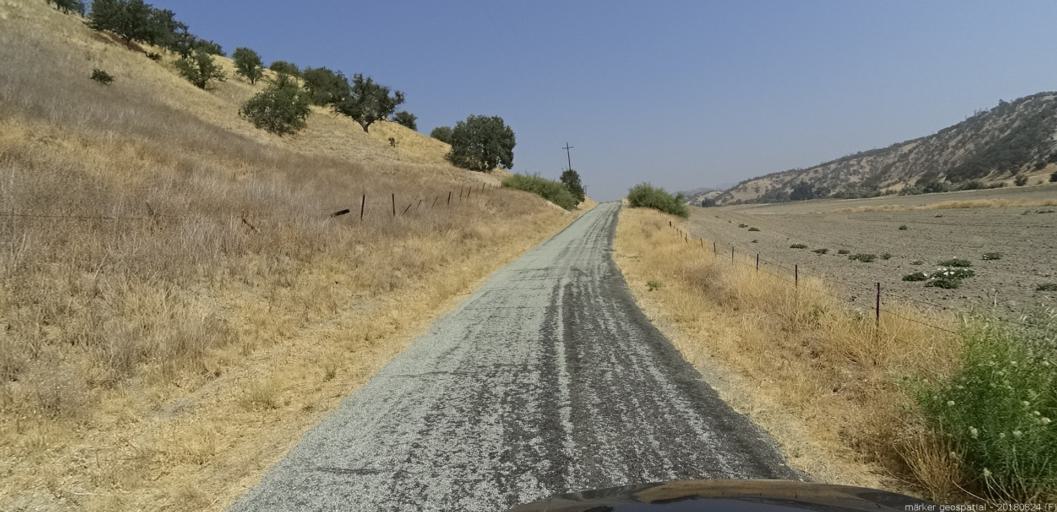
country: US
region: California
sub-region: San Luis Obispo County
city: San Miguel
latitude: 35.9772
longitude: -120.6463
